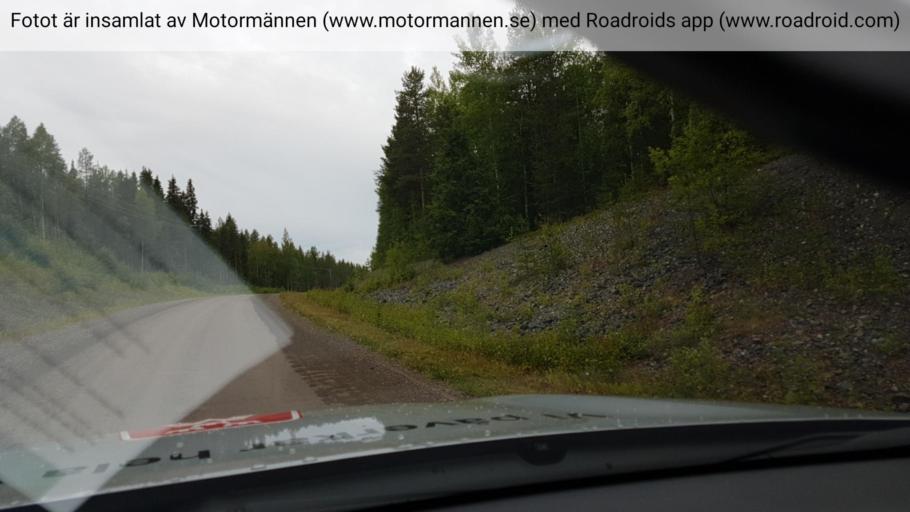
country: SE
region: Norrbotten
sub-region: Alvsbyns Kommun
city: AElvsbyn
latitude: 65.9985
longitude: 21.1633
